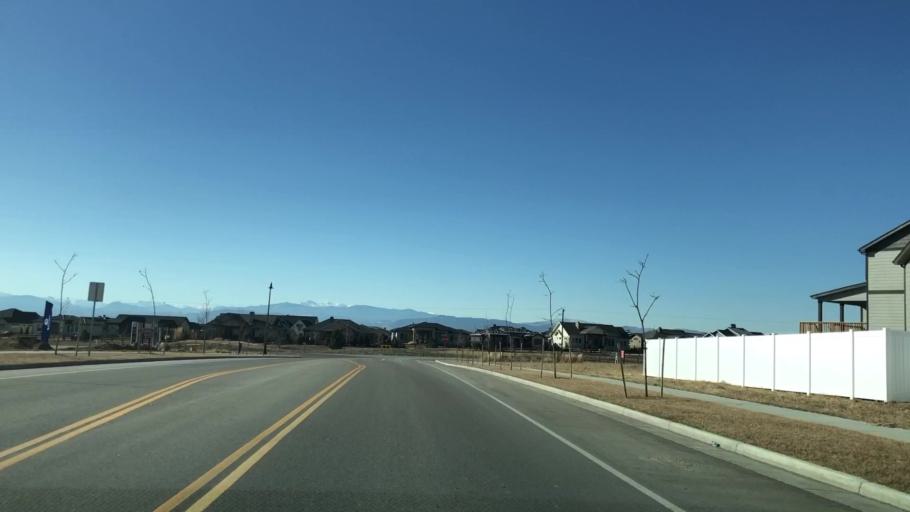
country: US
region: Colorado
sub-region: Weld County
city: Windsor
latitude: 40.5301
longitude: -104.9429
